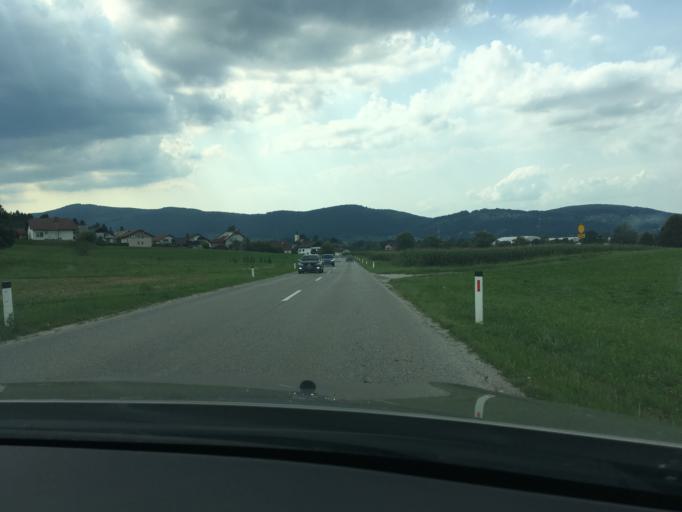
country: SI
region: Novo Mesto
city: Novo Mesto
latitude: 45.7926
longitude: 15.1302
